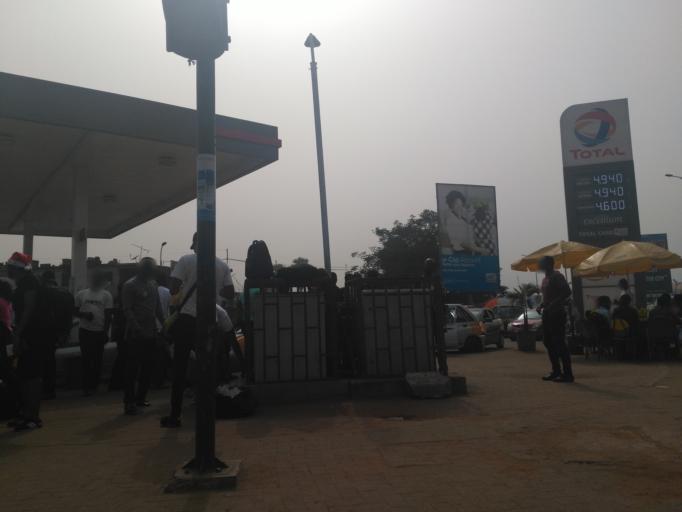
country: GH
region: Ashanti
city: Kumasi
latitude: 6.7082
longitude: -1.6371
